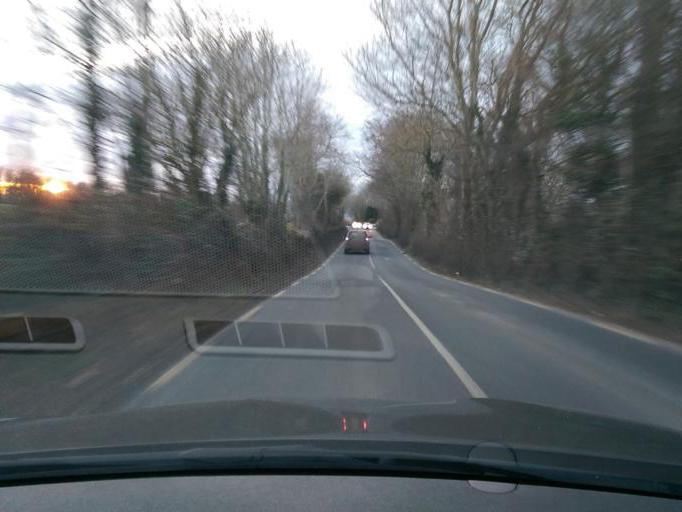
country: IE
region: Connaught
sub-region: County Galway
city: Portumna
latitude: 53.0986
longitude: -8.1704
